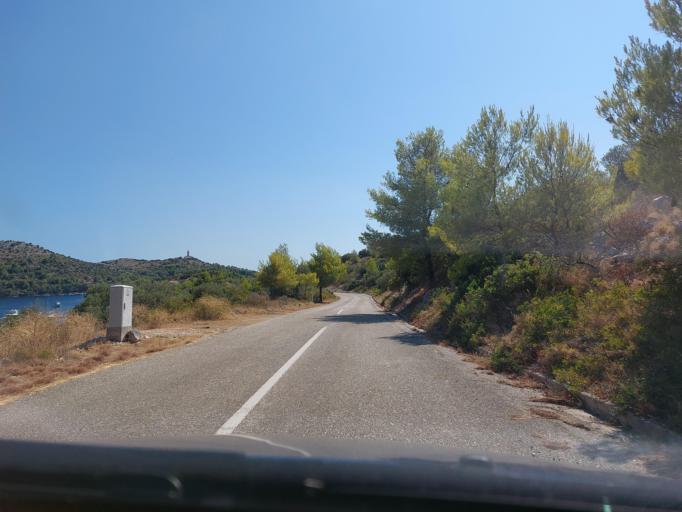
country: HR
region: Dubrovacko-Neretvanska
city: Smokvica
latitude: 42.7372
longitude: 16.8853
